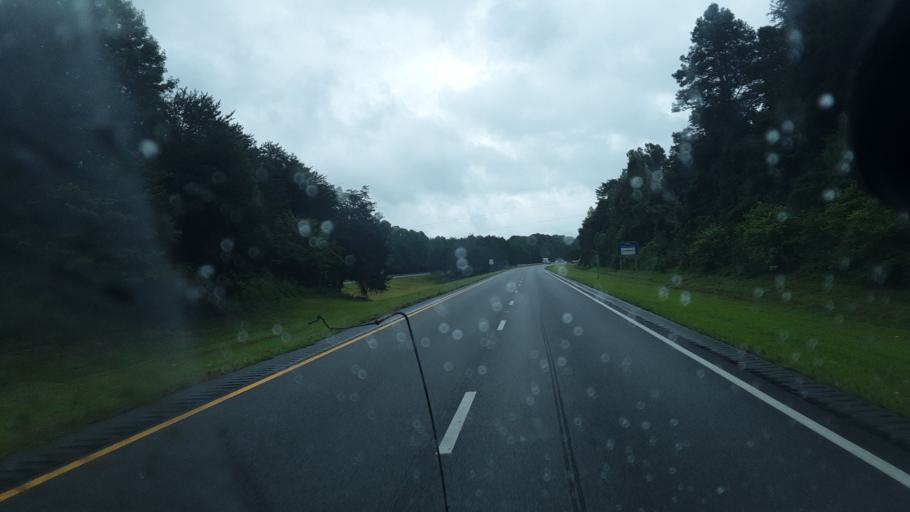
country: US
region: North Carolina
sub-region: Davidson County
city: Wallburg
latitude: 36.0546
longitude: -80.1458
